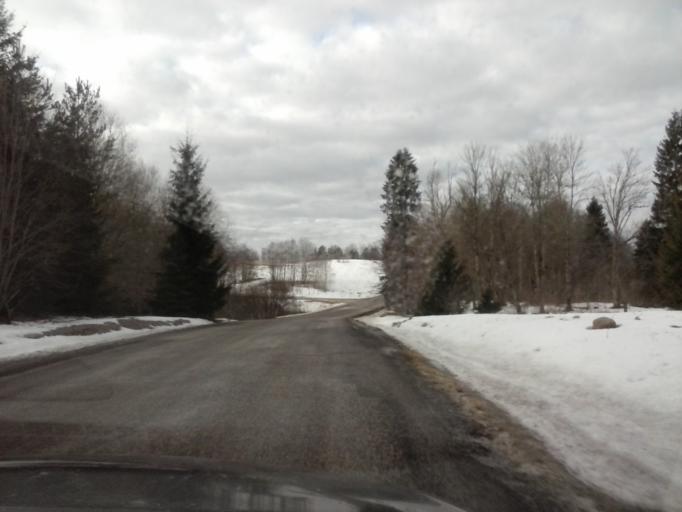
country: EE
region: Tartu
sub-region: Elva linn
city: Elva
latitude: 58.0225
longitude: 26.3354
